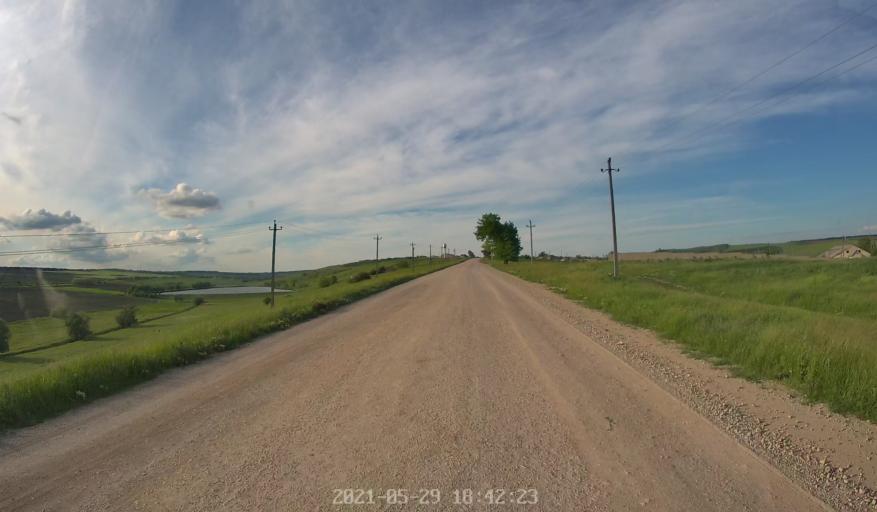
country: MD
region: Chisinau
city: Singera
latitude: 46.8118
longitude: 28.9619
